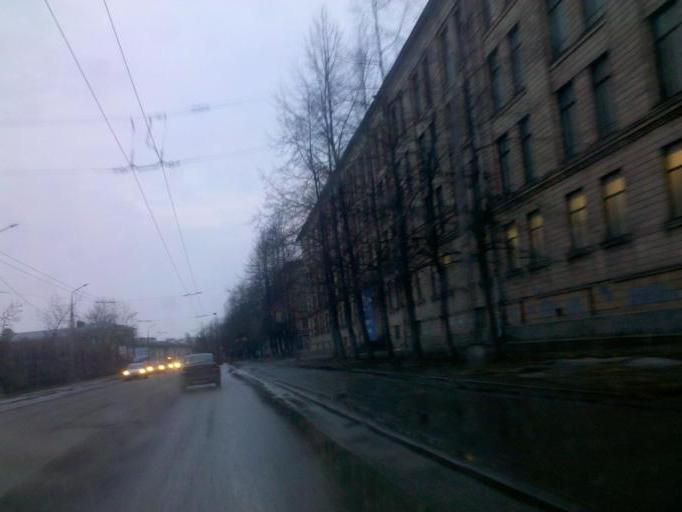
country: RU
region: Republic of Karelia
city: Petrozavodsk
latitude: 61.7841
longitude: 34.3814
